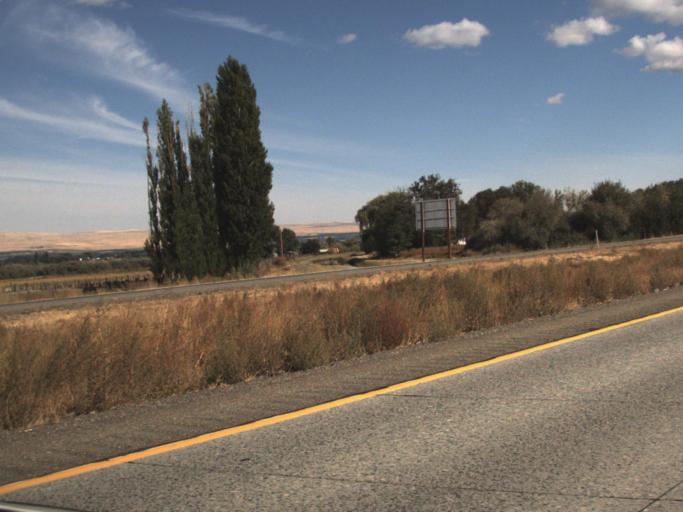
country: US
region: Washington
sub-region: Yakima County
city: Sunnyside
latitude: 46.3220
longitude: -120.0662
